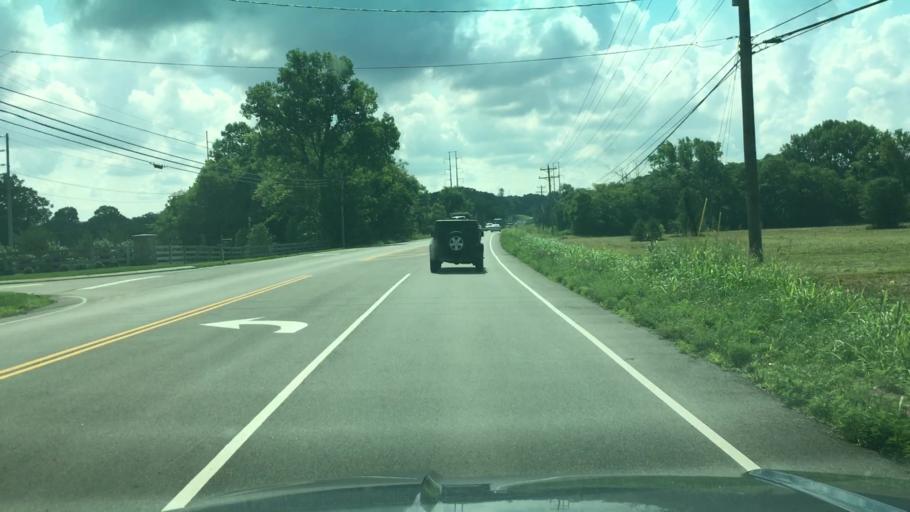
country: US
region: Tennessee
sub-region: Williamson County
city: Nolensville
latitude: 35.8677
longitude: -86.6992
